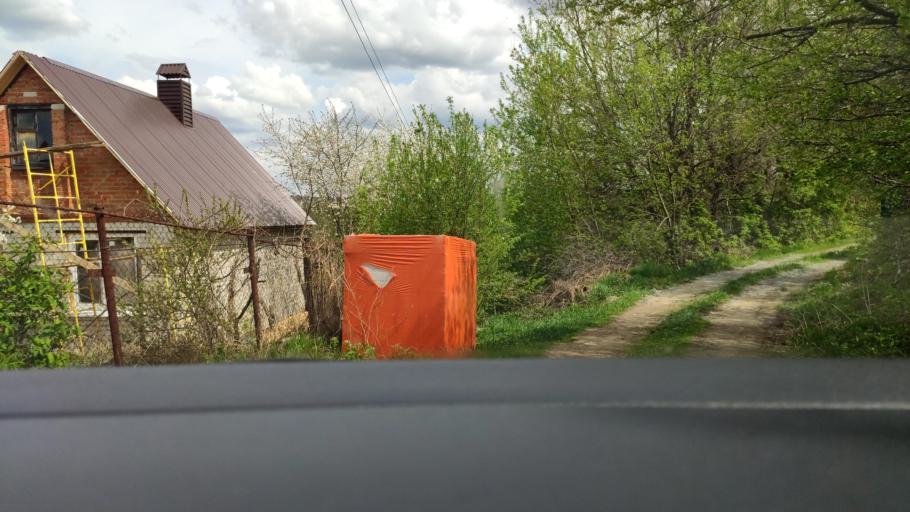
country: RU
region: Voronezj
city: Semiluki
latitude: 51.7816
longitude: 38.9981
